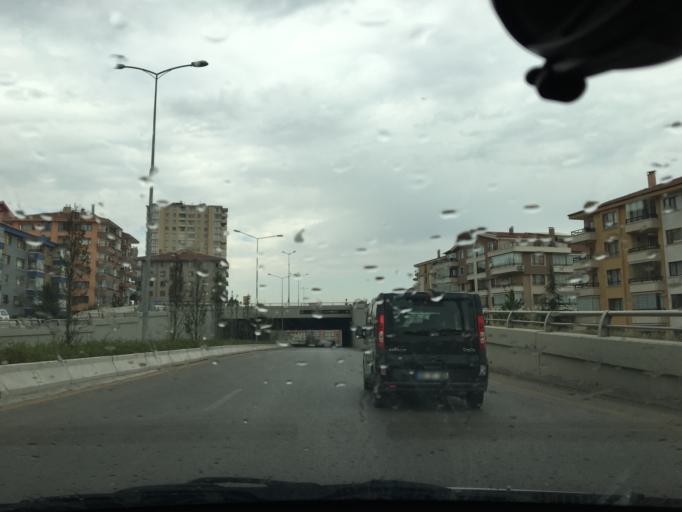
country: TR
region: Ankara
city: Ankara
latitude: 39.8842
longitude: 32.8304
